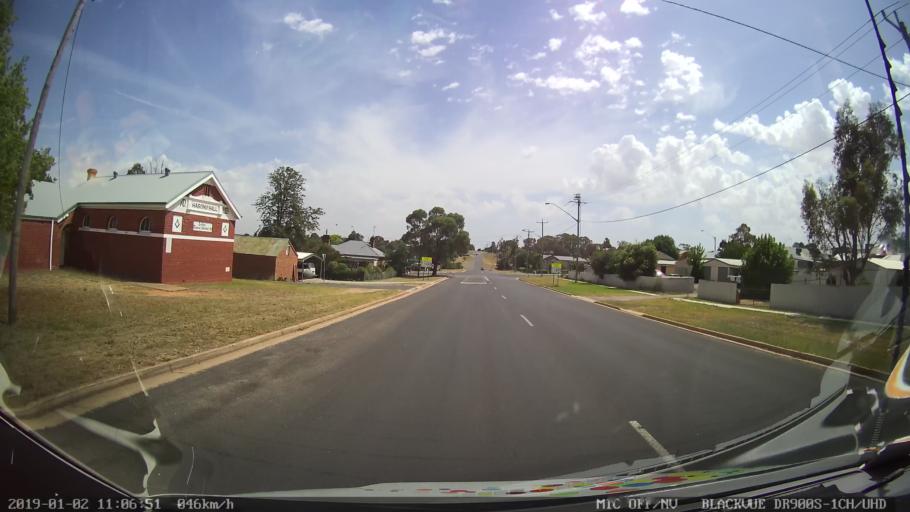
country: AU
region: New South Wales
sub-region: Young
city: Young
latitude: -34.5525
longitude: 148.3576
